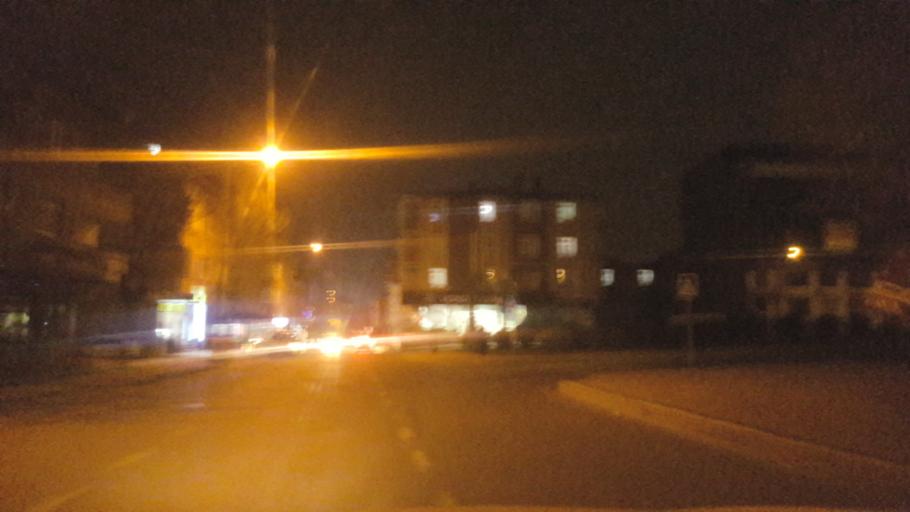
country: TR
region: Kocaeli
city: Darica
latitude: 40.7789
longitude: 29.3887
